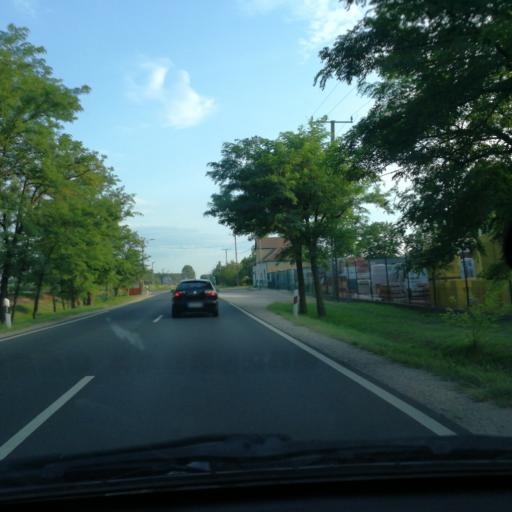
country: HU
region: Bacs-Kiskun
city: Kiskunfelegyhaza
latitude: 46.6728
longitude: 19.8213
